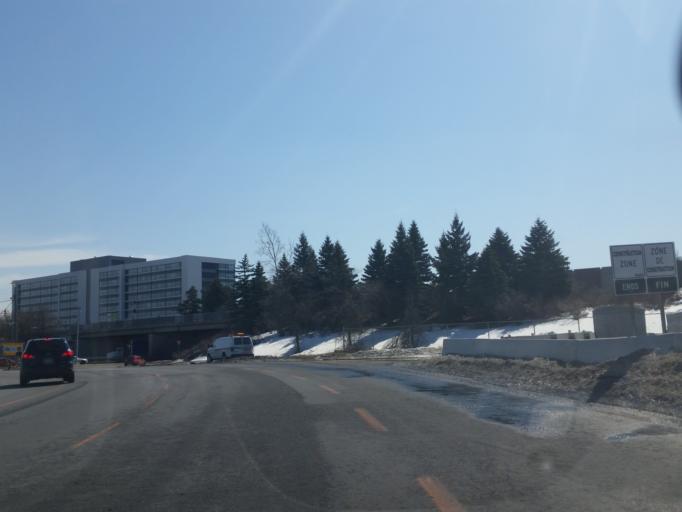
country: CA
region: Ontario
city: Ottawa
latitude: 45.4162
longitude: -75.6583
